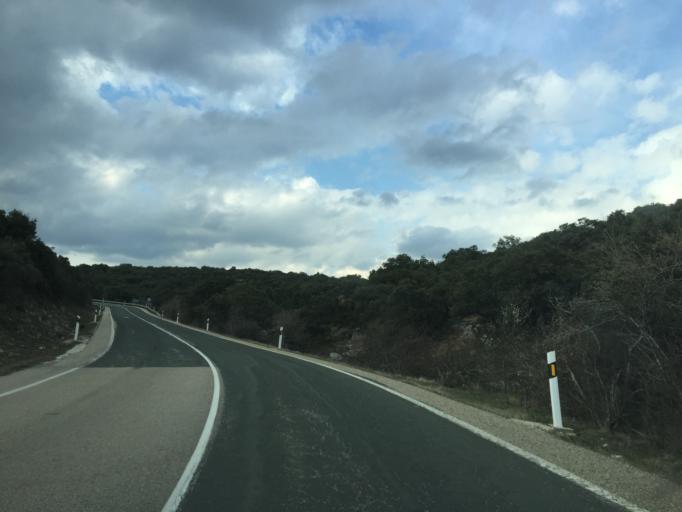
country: ES
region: Cantabria
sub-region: Provincia de Cantabria
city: San Martin de Elines
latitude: 42.8216
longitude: -3.7665
